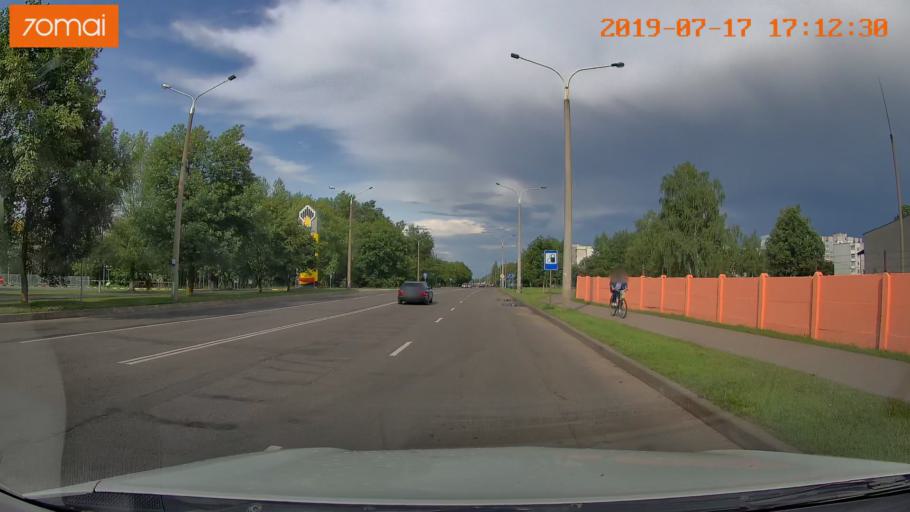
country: BY
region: Mogilev
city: Babruysk
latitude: 53.1722
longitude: 29.1793
